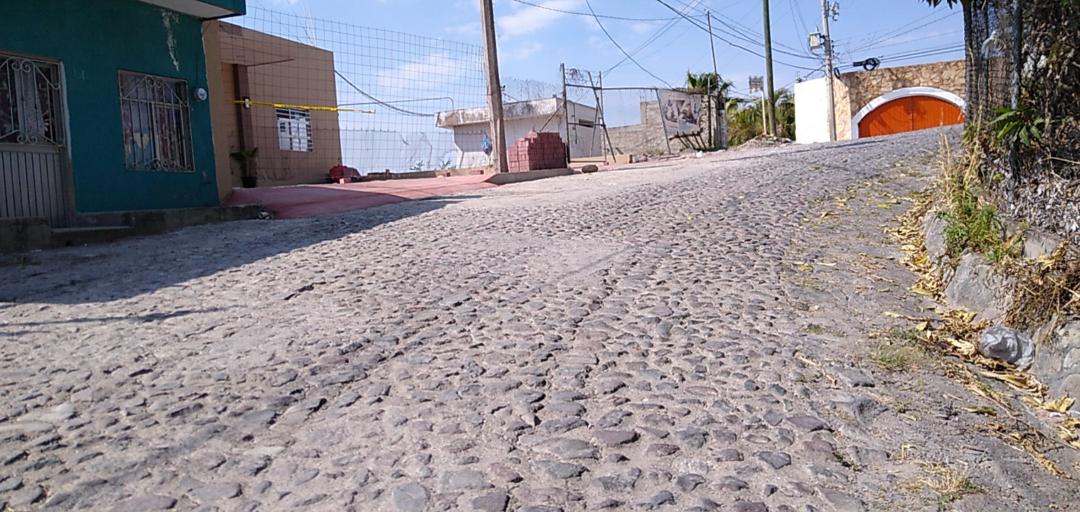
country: MX
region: Nayarit
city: Tepic
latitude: 21.5297
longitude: -104.9153
